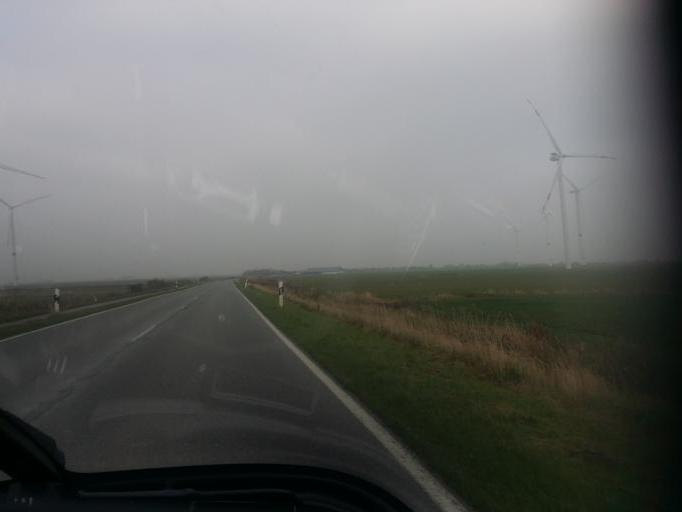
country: DE
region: Schleswig-Holstein
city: Ockholm
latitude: 54.6563
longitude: 8.8629
